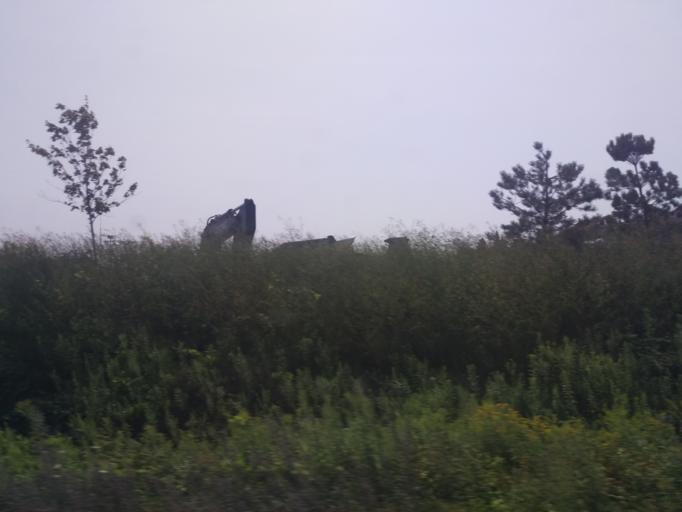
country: CA
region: Ontario
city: Ajax
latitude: 43.8389
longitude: -79.0681
